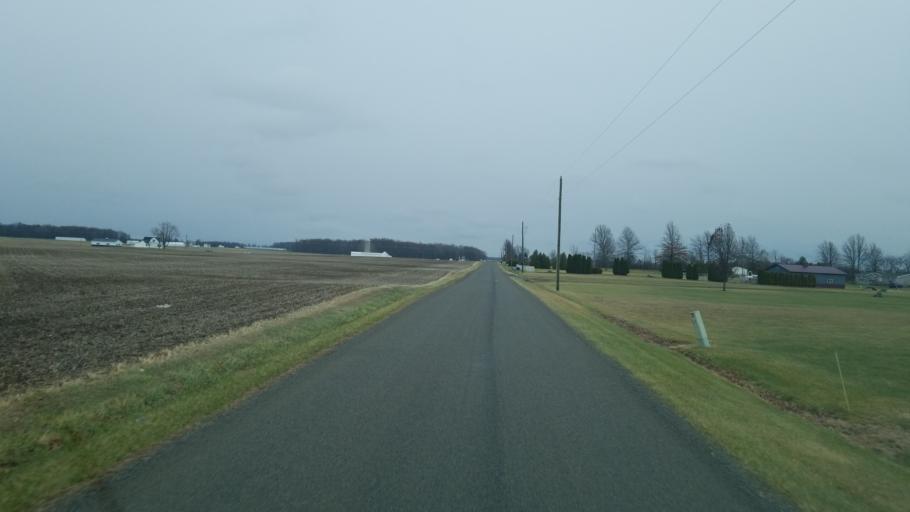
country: US
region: Ohio
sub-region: Union County
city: Marysville
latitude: 40.3308
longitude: -83.3643
